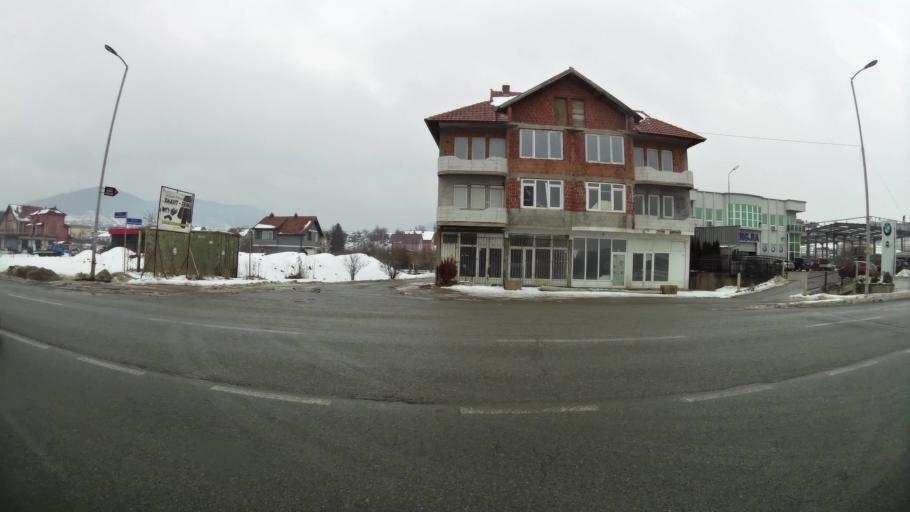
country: XK
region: Pristina
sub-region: Komuna e Prishtines
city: Pristina
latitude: 42.7077
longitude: 21.1540
